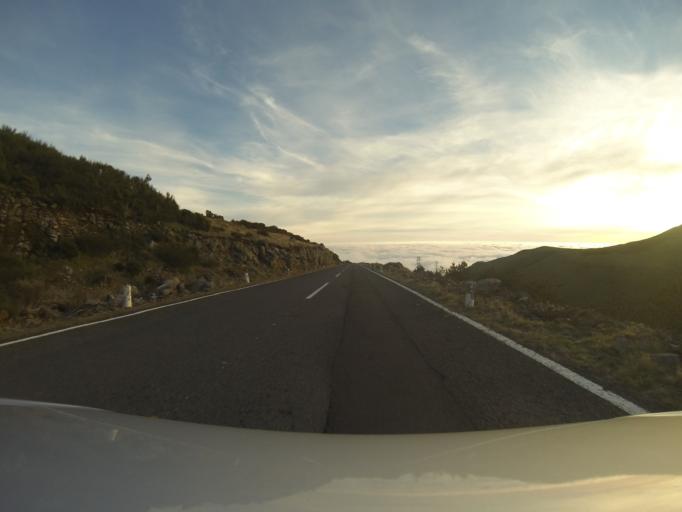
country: PT
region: Madeira
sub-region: Sao Vicente
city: Sao Vicente
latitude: 32.7357
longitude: -17.0614
